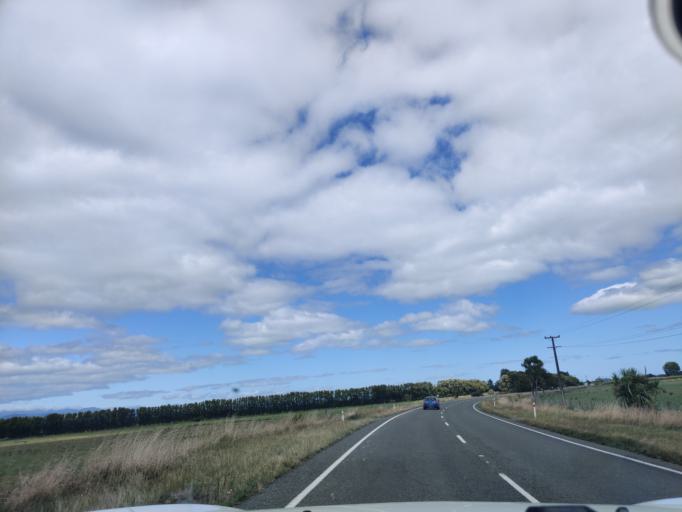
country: NZ
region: Manawatu-Wanganui
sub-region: Palmerston North City
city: Palmerston North
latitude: -40.4194
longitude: 175.4728
